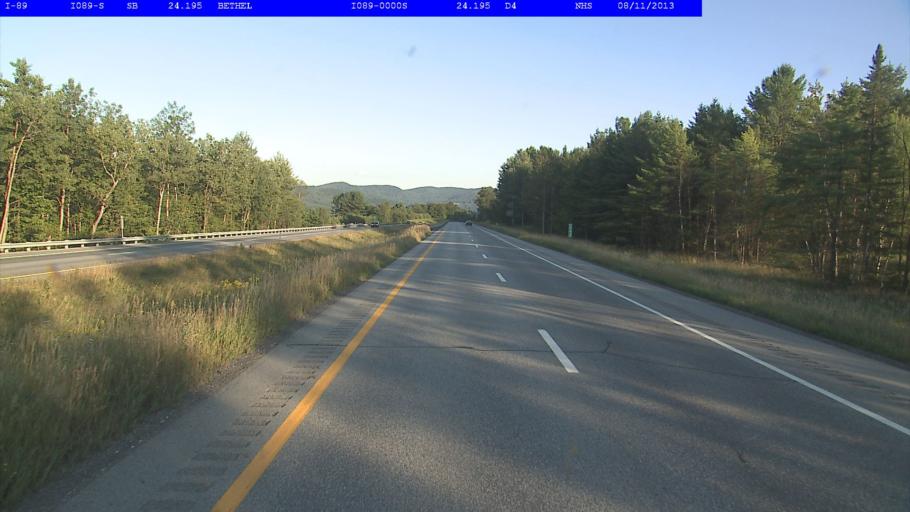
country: US
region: Vermont
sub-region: Orange County
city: Randolph
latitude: 43.8508
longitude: -72.6034
